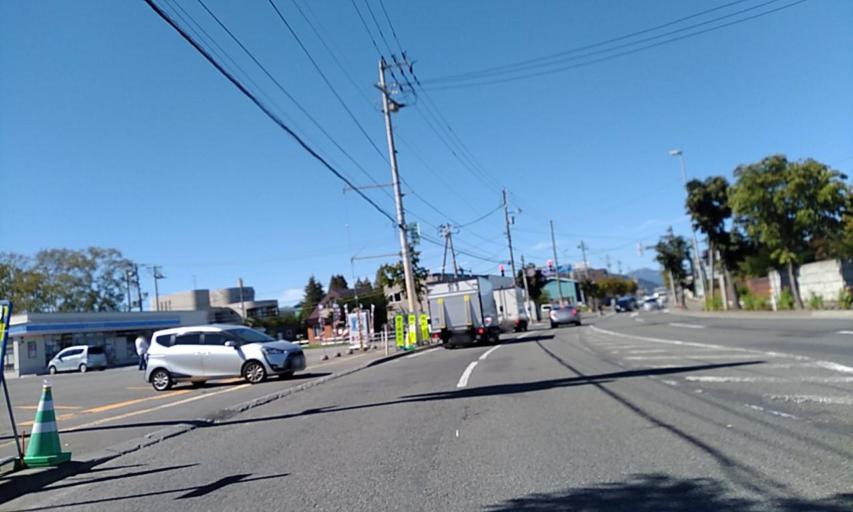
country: JP
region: Hokkaido
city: Sapporo
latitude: 43.0028
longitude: 141.3919
